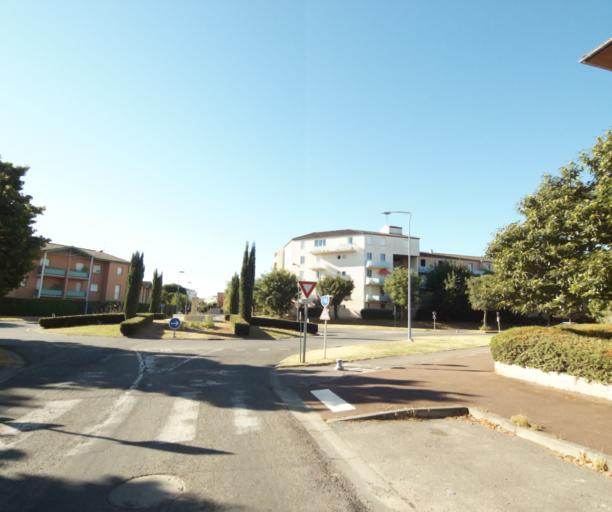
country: FR
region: Midi-Pyrenees
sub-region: Departement de la Haute-Garonne
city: Castanet-Tolosan
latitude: 43.5201
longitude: 1.5081
